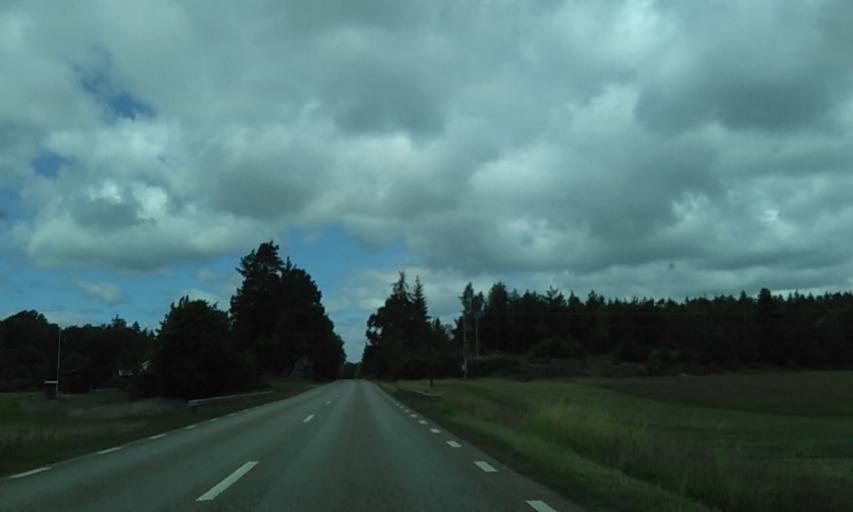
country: SE
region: Vaestra Goetaland
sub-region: Essunga Kommun
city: Nossebro
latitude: 58.2545
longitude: 12.6930
